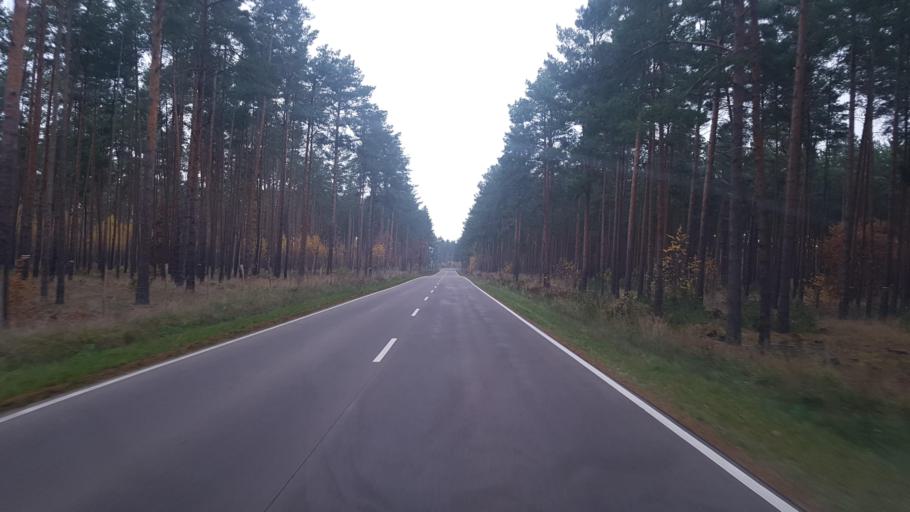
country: DE
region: Brandenburg
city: Gross Kreutz
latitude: 52.3518
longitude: 12.7786
